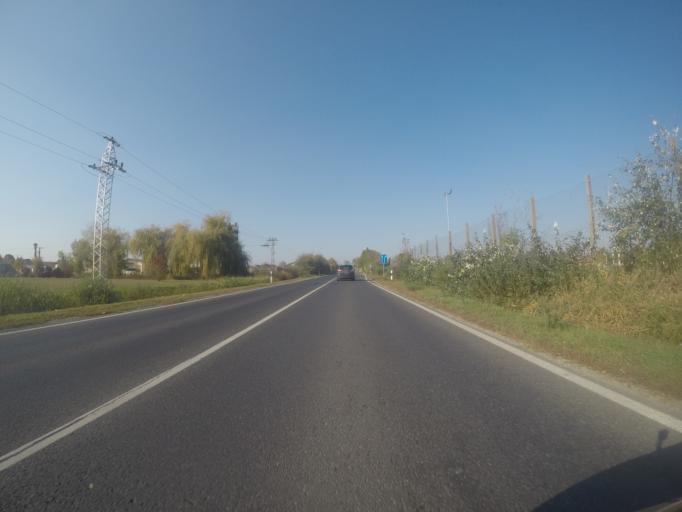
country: HU
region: Tolna
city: Dunafoldvar
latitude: 46.8105
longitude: 18.9113
